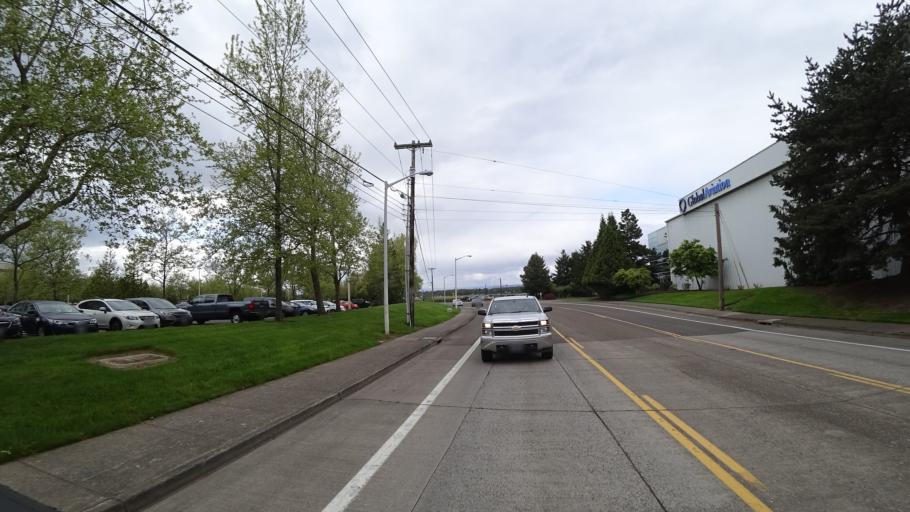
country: US
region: Oregon
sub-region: Washington County
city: Hillsboro
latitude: 45.5429
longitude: -122.9572
